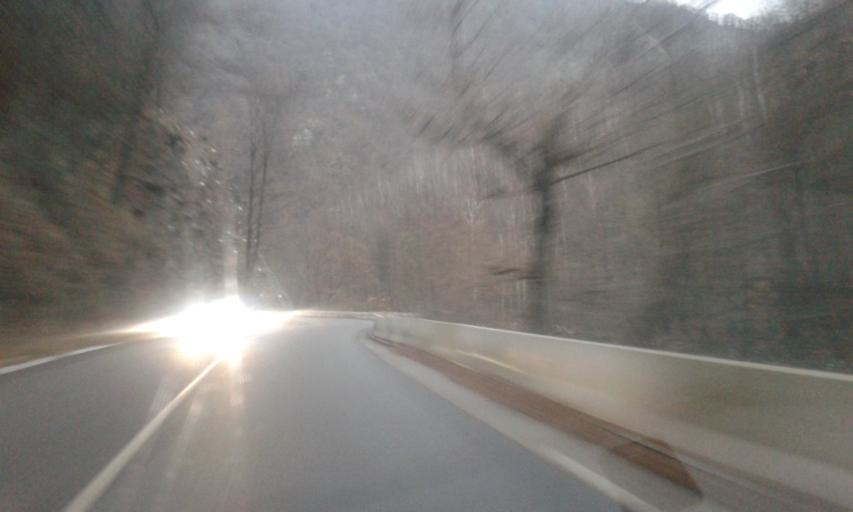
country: RO
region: Gorj
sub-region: Comuna Bumbesti-Jiu
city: Bumbesti-Jiu
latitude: 45.2498
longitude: 23.3872
